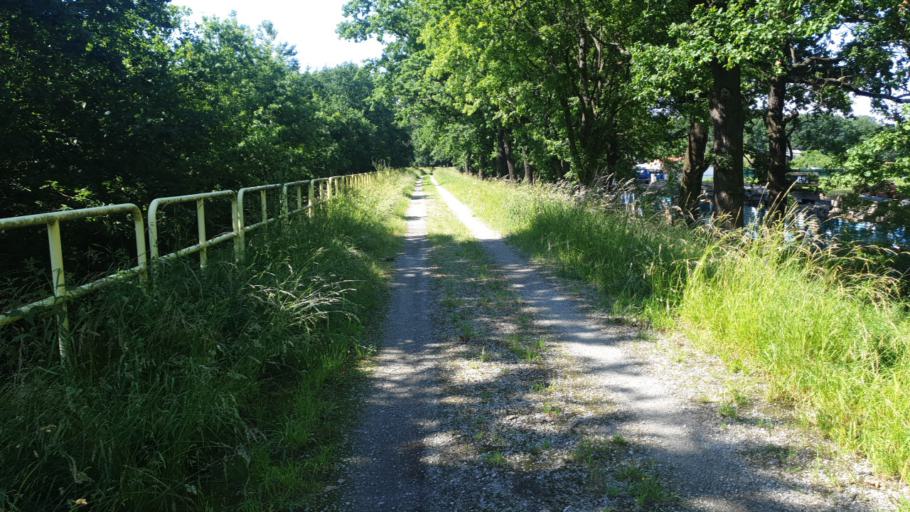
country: PL
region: Lower Silesian Voivodeship
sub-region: Powiat wroclawski
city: Radwanice
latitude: 51.0924
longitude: 17.1150
